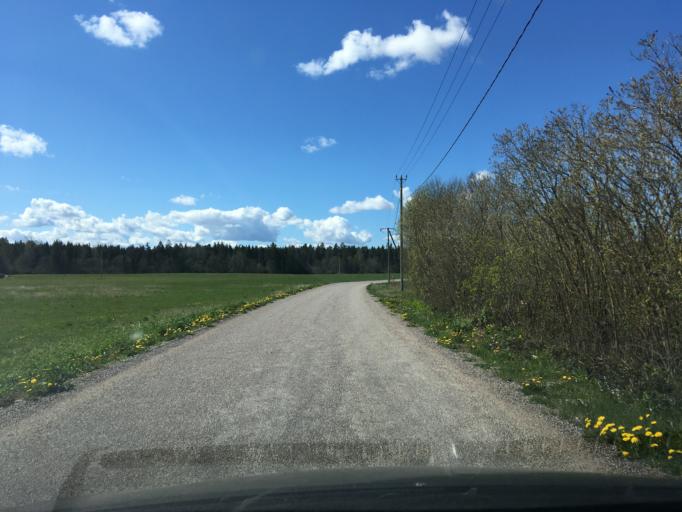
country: EE
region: Harju
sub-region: Rae vald
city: Vaida
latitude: 59.2007
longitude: 25.0880
